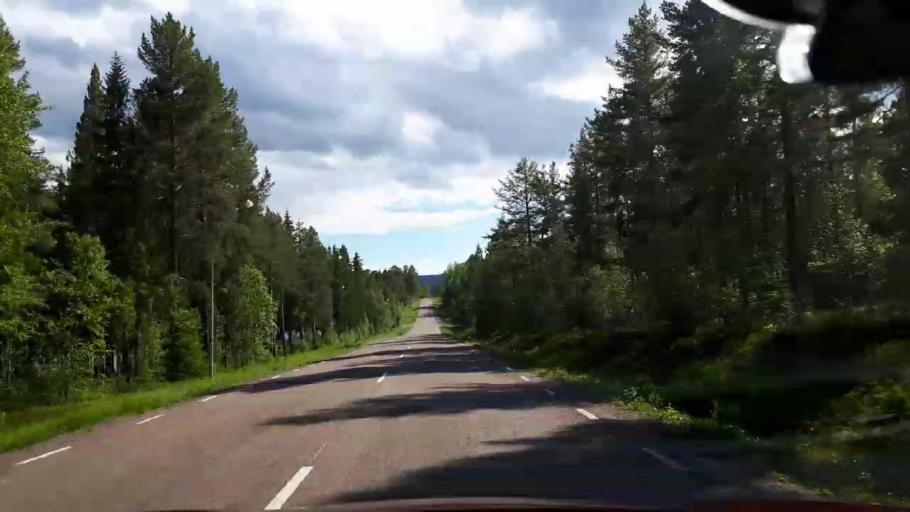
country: SE
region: Jaemtland
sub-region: Krokoms Kommun
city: Valla
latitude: 63.9830
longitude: 14.2222
